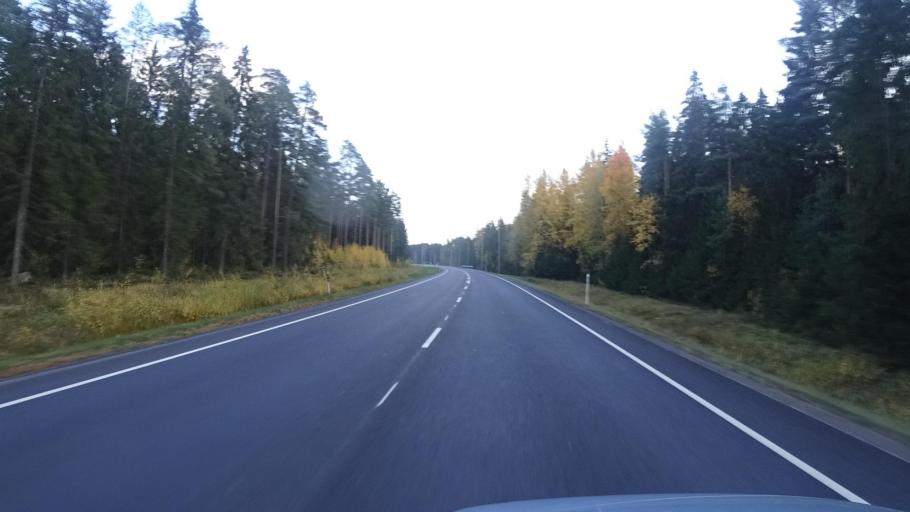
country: FI
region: Satakunta
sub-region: Rauma
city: Koeylioe
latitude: 61.0925
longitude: 22.2425
